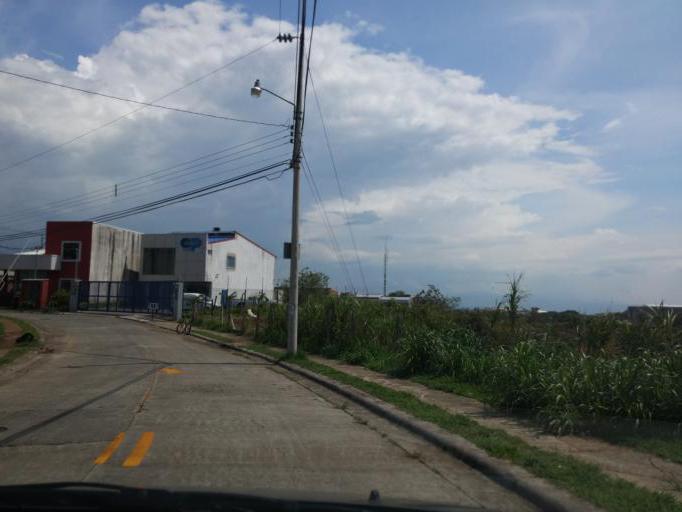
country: CR
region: Alajuela
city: Alajuela
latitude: 10.0156
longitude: -84.1993
